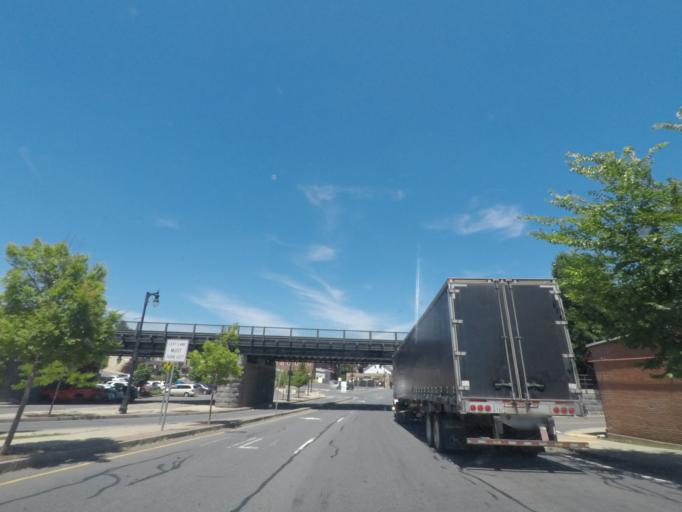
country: US
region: Massachusetts
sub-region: Hampden County
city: Westfield
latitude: 42.1295
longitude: -72.7451
